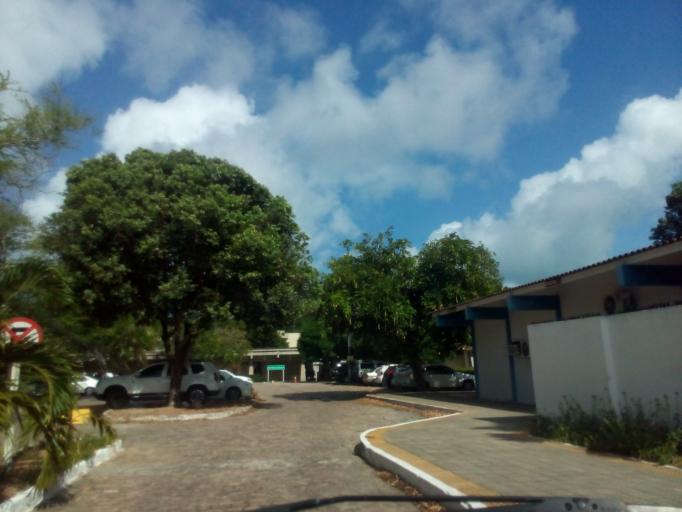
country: BR
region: Rio Grande do Norte
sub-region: Natal
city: Natal
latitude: -5.8384
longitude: -35.1986
